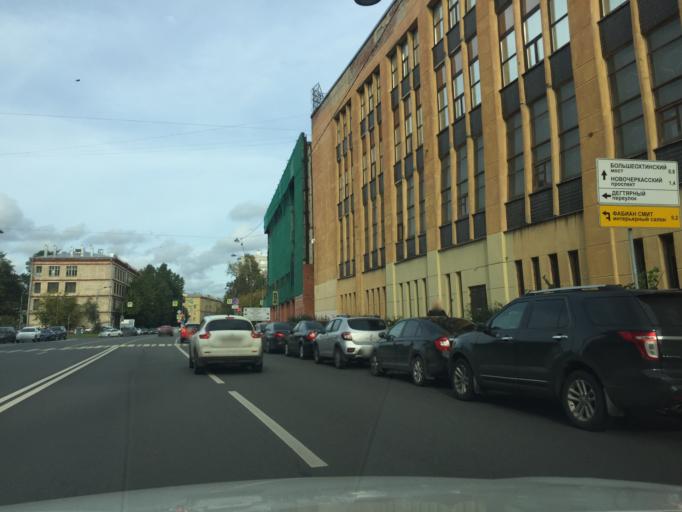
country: RU
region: St.-Petersburg
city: Centralniy
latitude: 59.9386
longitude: 30.3879
